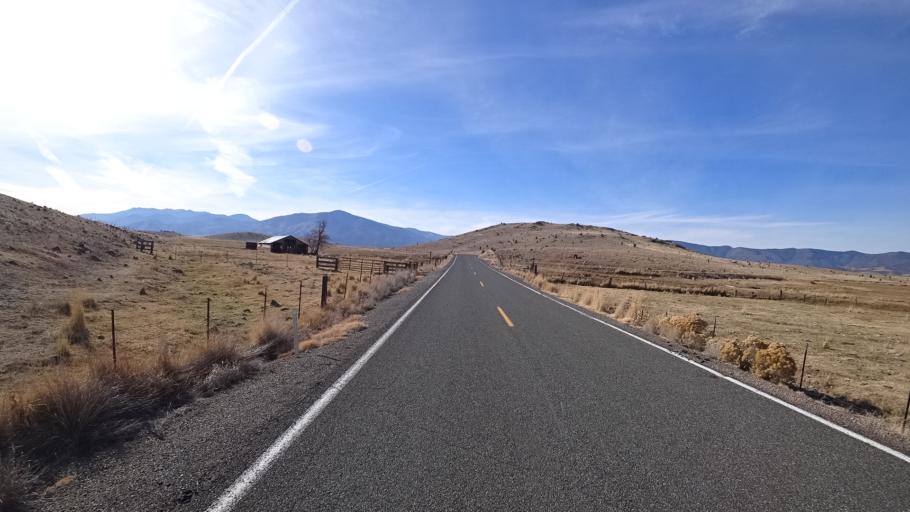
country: US
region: California
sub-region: Siskiyou County
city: Weed
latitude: 41.5486
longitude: -122.4965
